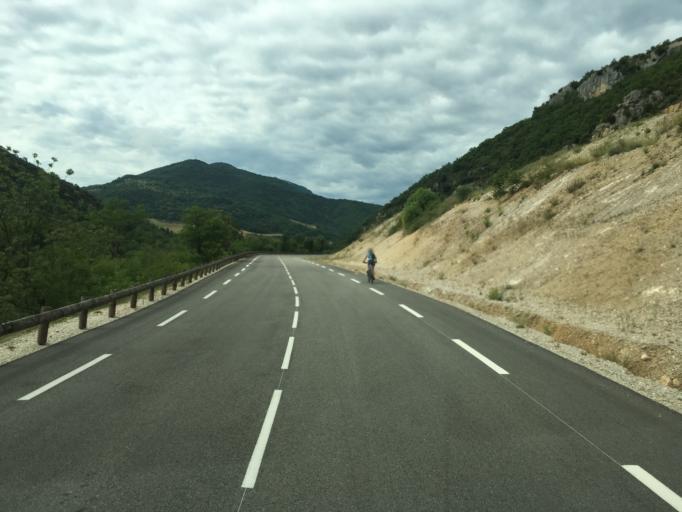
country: FR
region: Rhone-Alpes
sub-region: Departement de la Drome
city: Nyons
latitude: 44.3952
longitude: 5.2342
